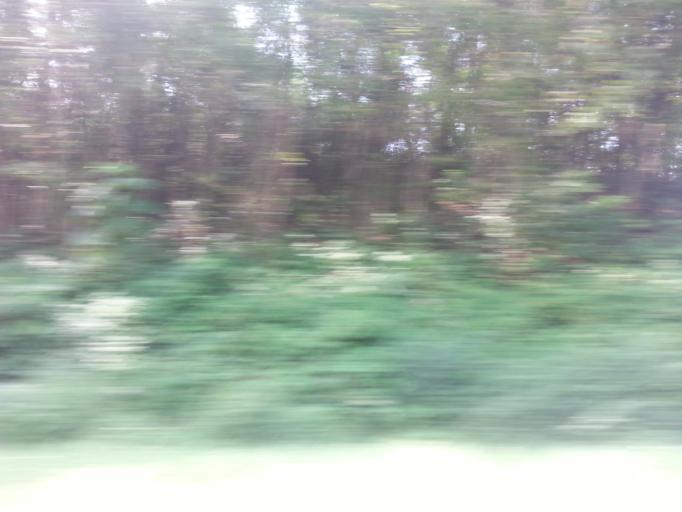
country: US
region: Tennessee
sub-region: Roane County
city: Rockwood
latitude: 35.8883
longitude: -84.6916
